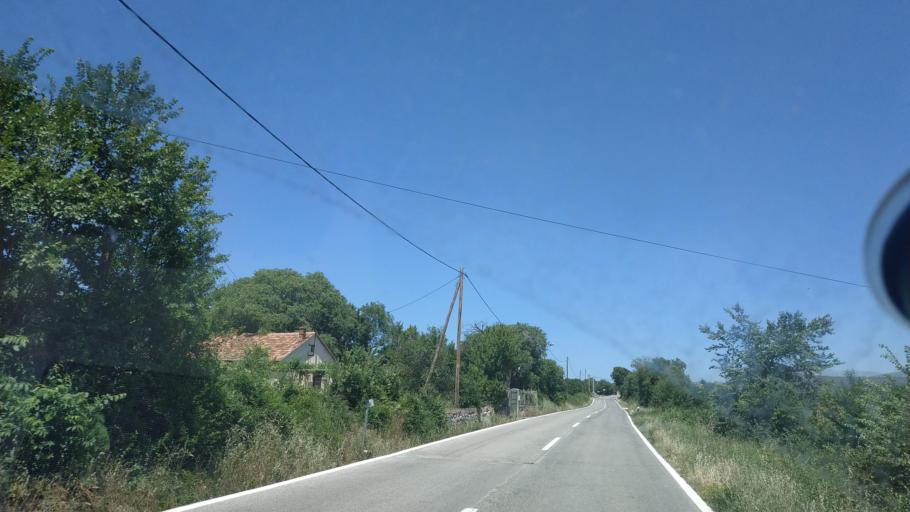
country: HR
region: Sibensko-Kniniska
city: Drnis
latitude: 43.8826
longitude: 16.2048
